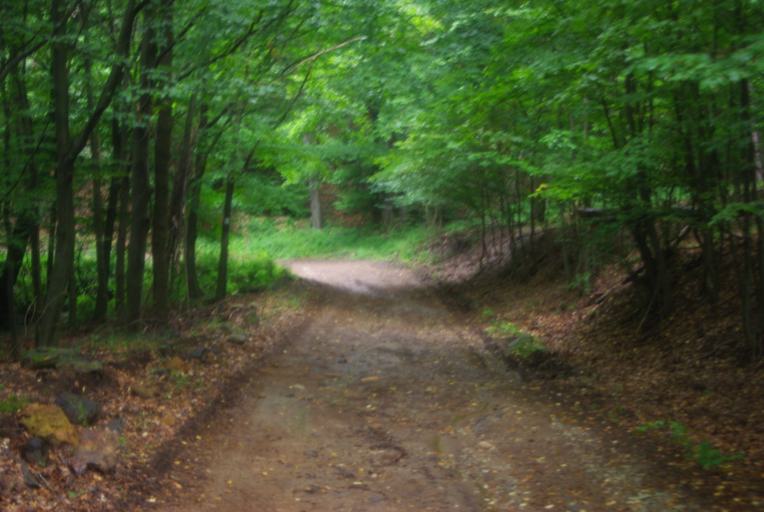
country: HU
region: Borsod-Abauj-Zemplen
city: Gonc
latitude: 48.3985
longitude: 21.3637
